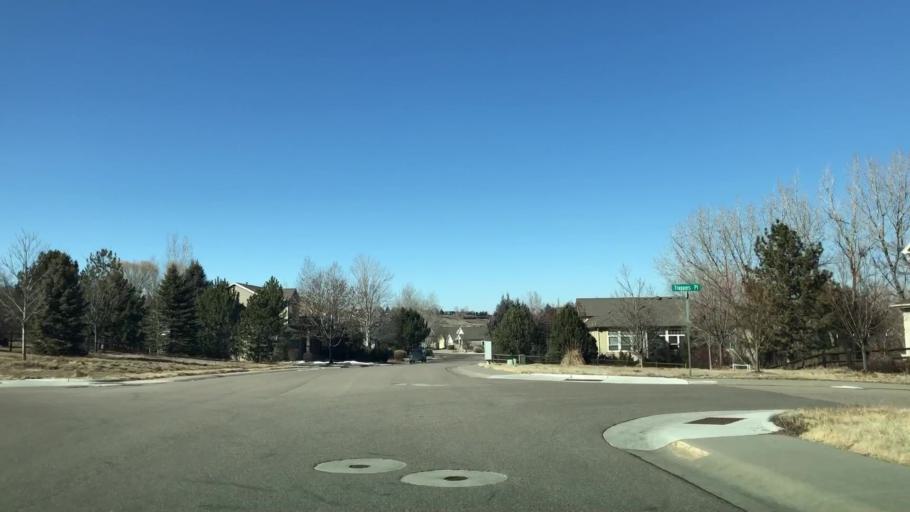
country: US
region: Colorado
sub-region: Weld County
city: Windsor
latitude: 40.4726
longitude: -104.9494
